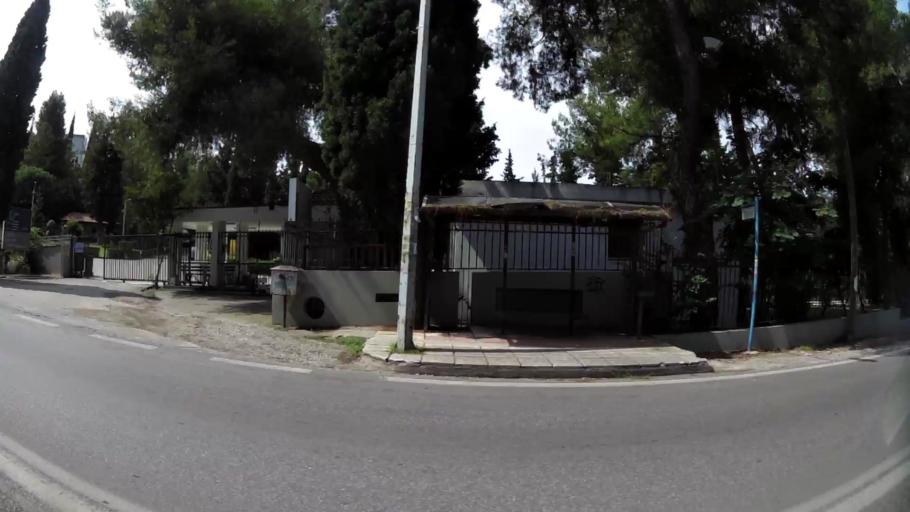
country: GR
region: Central Macedonia
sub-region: Nomos Thessalonikis
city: Pylaia
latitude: 40.5961
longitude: 23.0041
